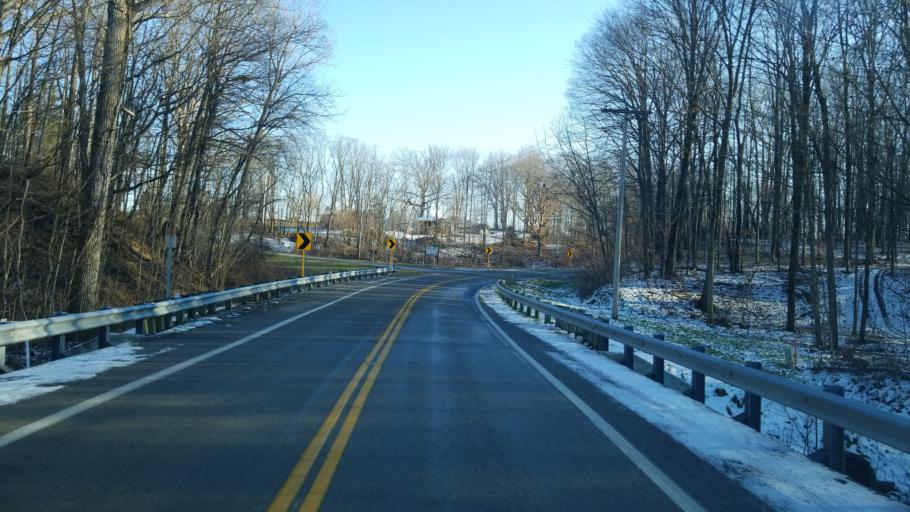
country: US
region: Ohio
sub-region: Sandusky County
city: Green Springs
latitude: 41.2282
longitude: -83.0166
